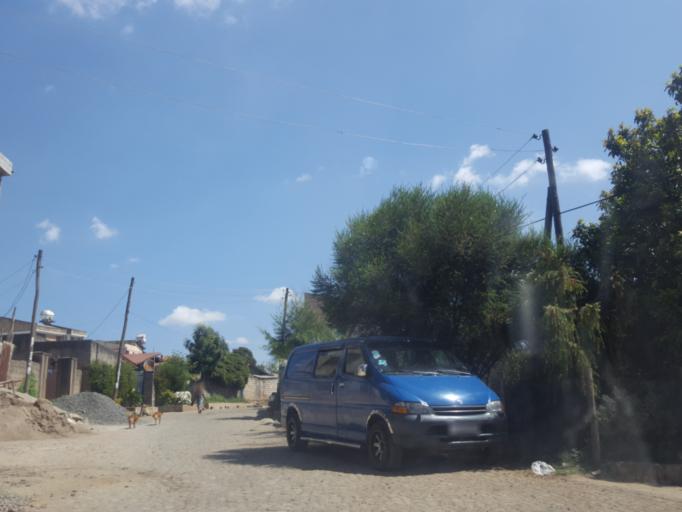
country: ET
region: Adis Abeba
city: Addis Ababa
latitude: 9.0600
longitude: 38.7315
